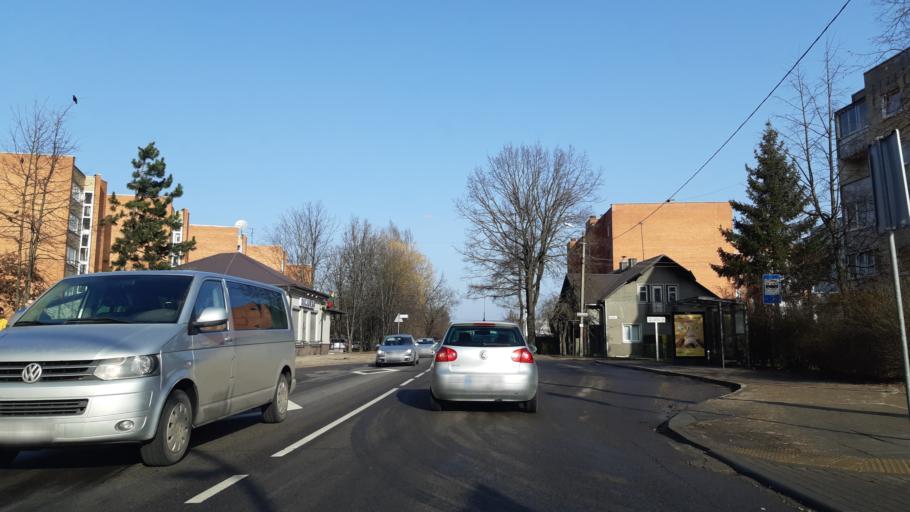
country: LT
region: Kauno apskritis
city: Dainava (Kaunas)
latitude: 54.9098
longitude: 23.9558
